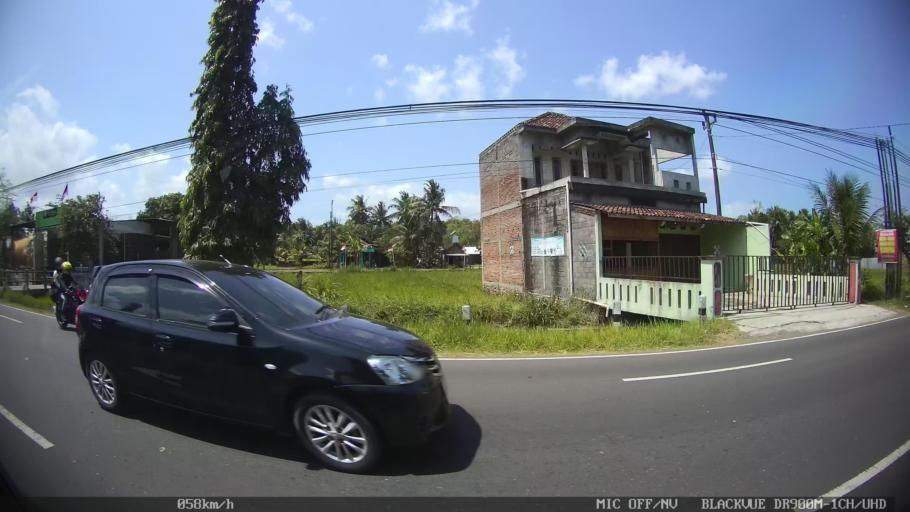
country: ID
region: Daerah Istimewa Yogyakarta
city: Pandak
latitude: -7.9256
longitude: 110.2784
